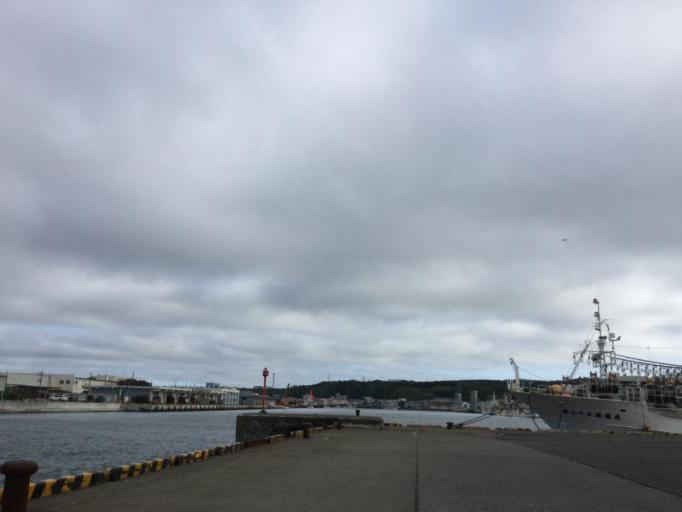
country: JP
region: Hokkaido
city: Wakkanai
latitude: 45.4113
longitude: 141.6781
